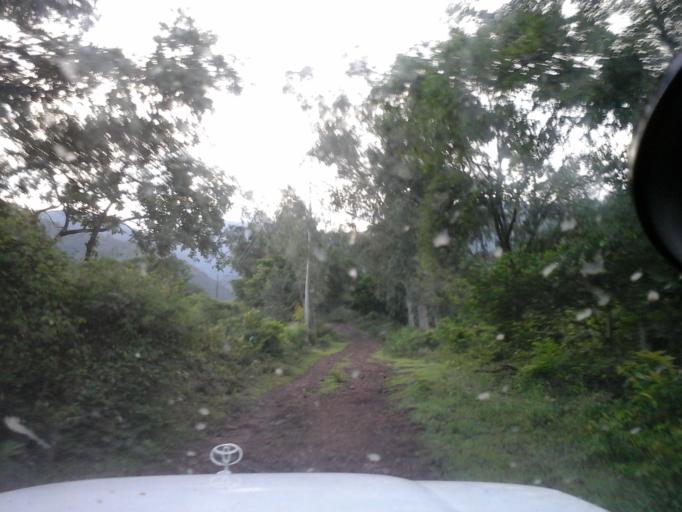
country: CO
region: Cesar
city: Agustin Codazzi
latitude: 10.1734
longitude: -73.1510
